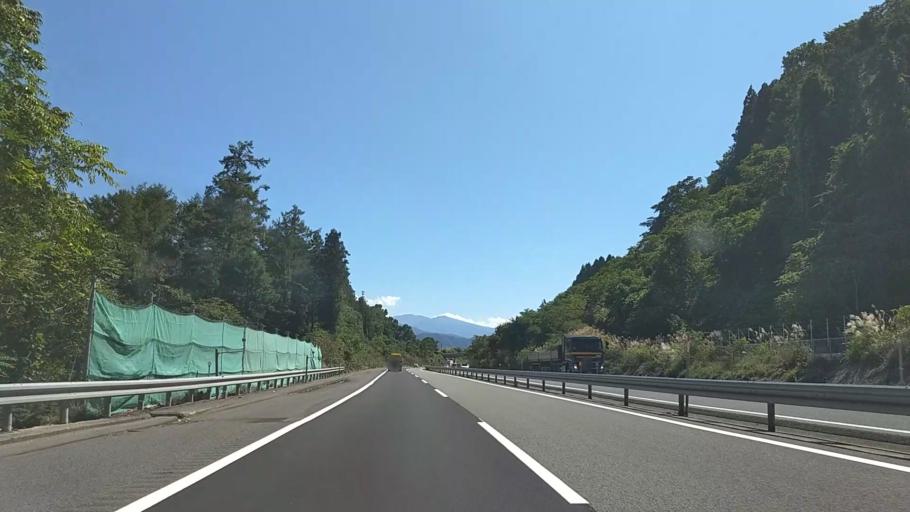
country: JP
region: Nagano
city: Nakano
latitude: 36.7786
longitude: 138.3176
